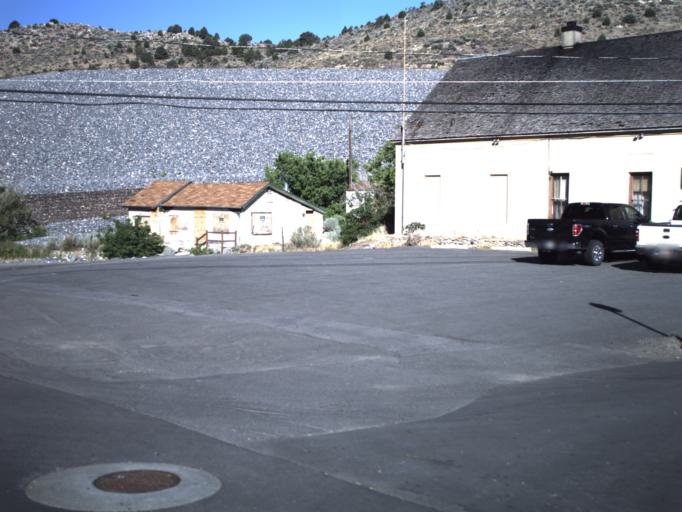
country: US
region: Utah
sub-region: Utah County
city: Genola
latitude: 39.9536
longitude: -112.1224
